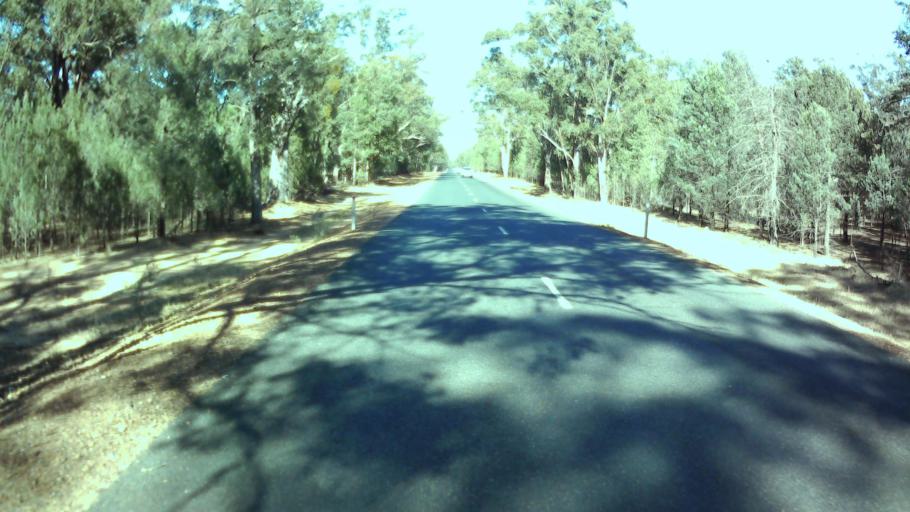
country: AU
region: New South Wales
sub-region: Weddin
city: Grenfell
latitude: -34.0240
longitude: 148.0231
